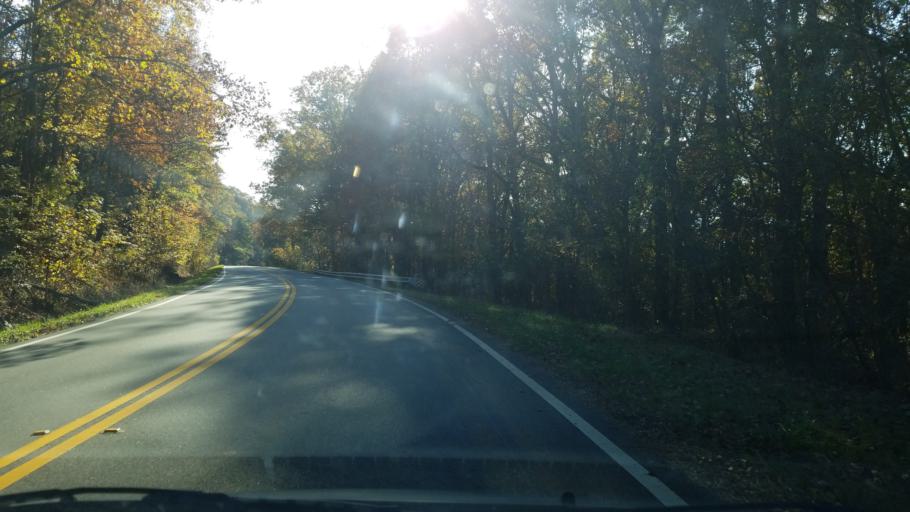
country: US
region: Georgia
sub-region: Dade County
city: Trenton
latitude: 34.8488
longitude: -85.4953
